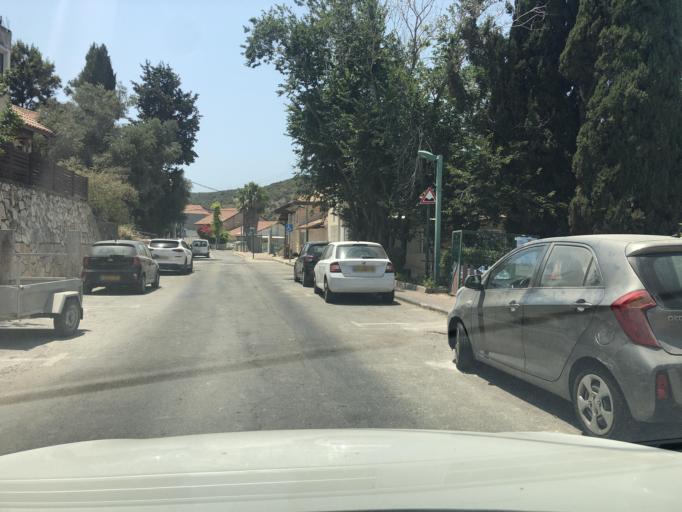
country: IL
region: Haifa
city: Daliyat el Karmil
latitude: 32.6619
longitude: 35.1096
